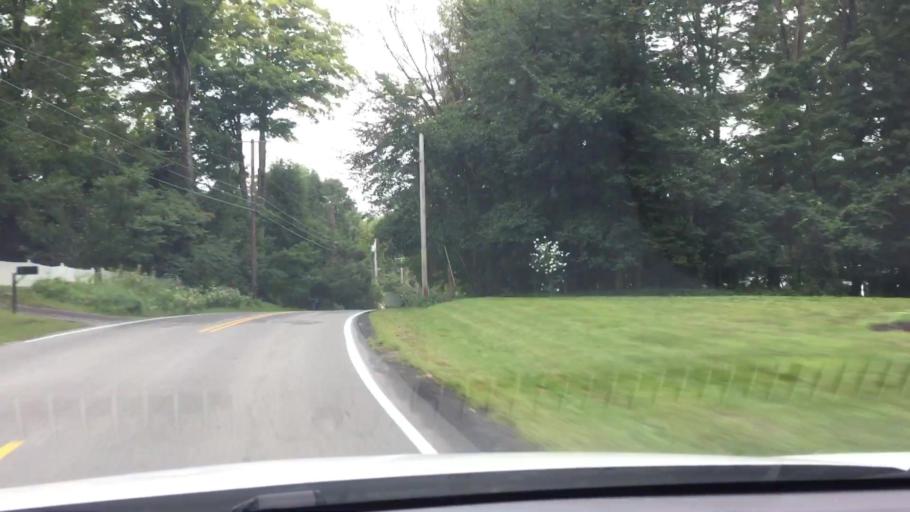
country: US
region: Massachusetts
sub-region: Berkshire County
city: Housatonic
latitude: 42.2646
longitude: -73.3806
